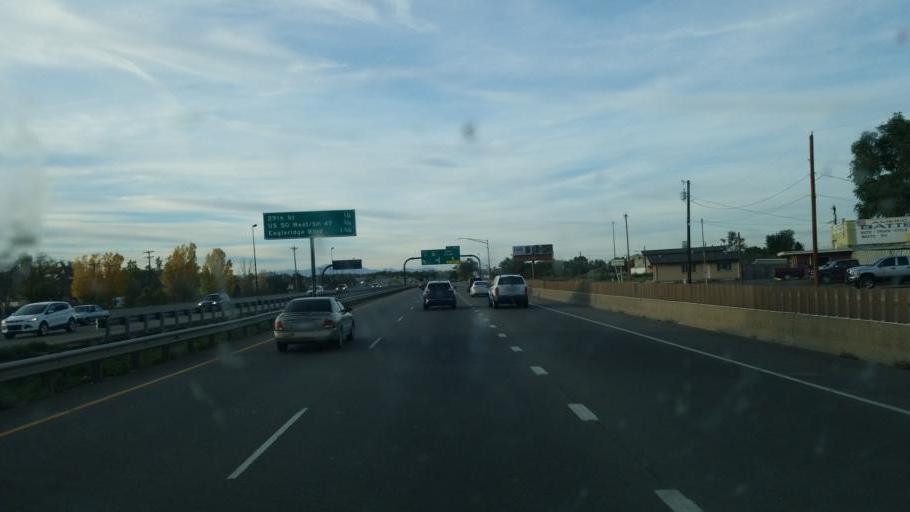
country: US
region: Colorado
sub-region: Pueblo County
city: Pueblo
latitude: 38.2925
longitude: -104.6084
